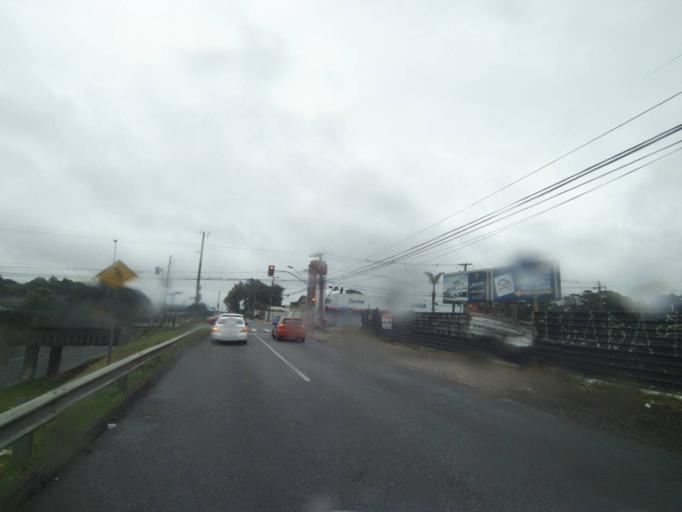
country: BR
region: Parana
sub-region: Curitiba
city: Curitiba
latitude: -25.4303
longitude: -49.3530
